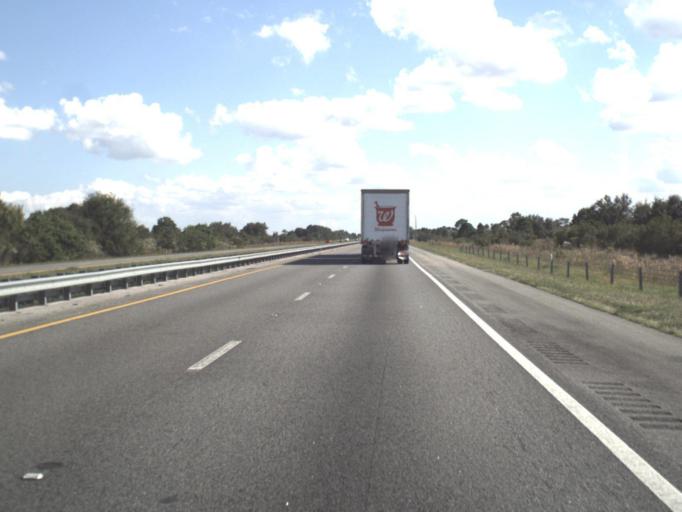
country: US
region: Florida
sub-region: Indian River County
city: Fellsmere
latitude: 27.7945
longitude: -80.9869
